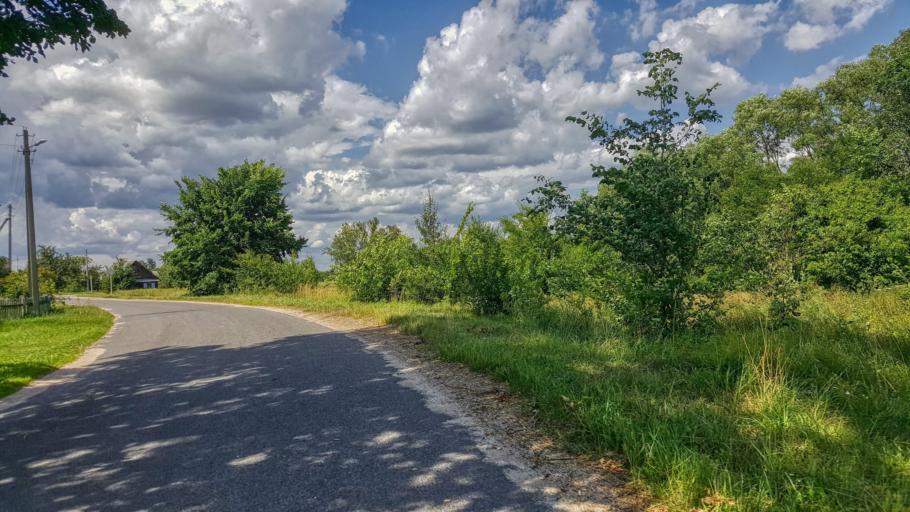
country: BY
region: Brest
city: Kamyanyets
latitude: 52.4178
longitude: 23.8878
